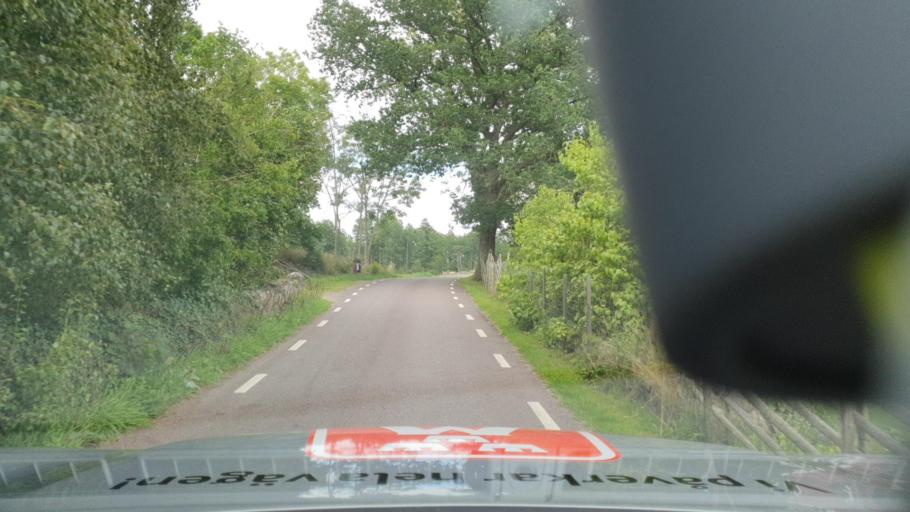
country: SE
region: Kalmar
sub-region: Kalmar Kommun
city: Lindsdal
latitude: 56.7687
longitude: 16.2296
